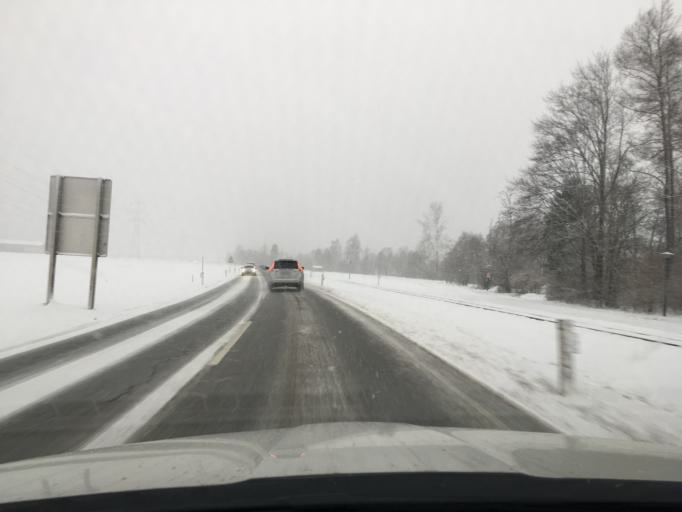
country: AT
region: Tyrol
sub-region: Politischer Bezirk Schwaz
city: Schwendau
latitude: 47.1884
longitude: 11.8666
